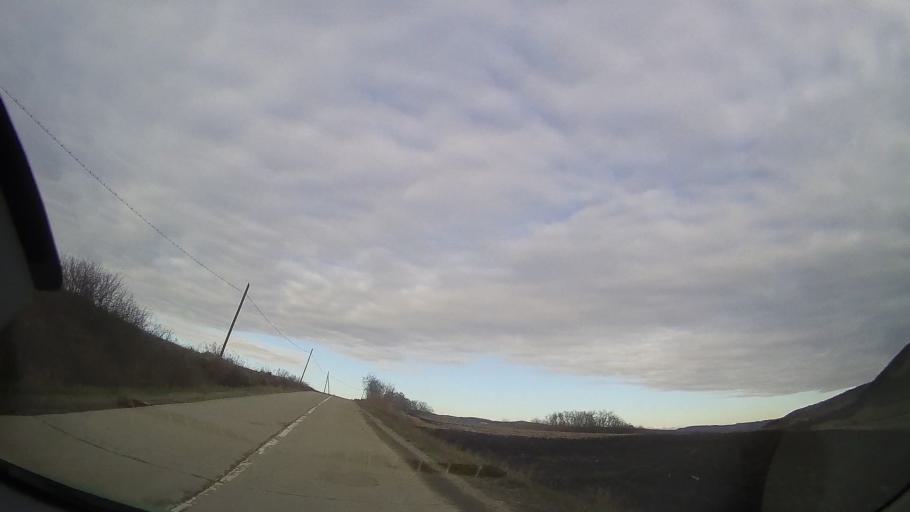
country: RO
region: Bistrita-Nasaud
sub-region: Comuna Sanmihaiu de Campie
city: Sanmihaiu de Campie
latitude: 46.8843
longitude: 24.3329
